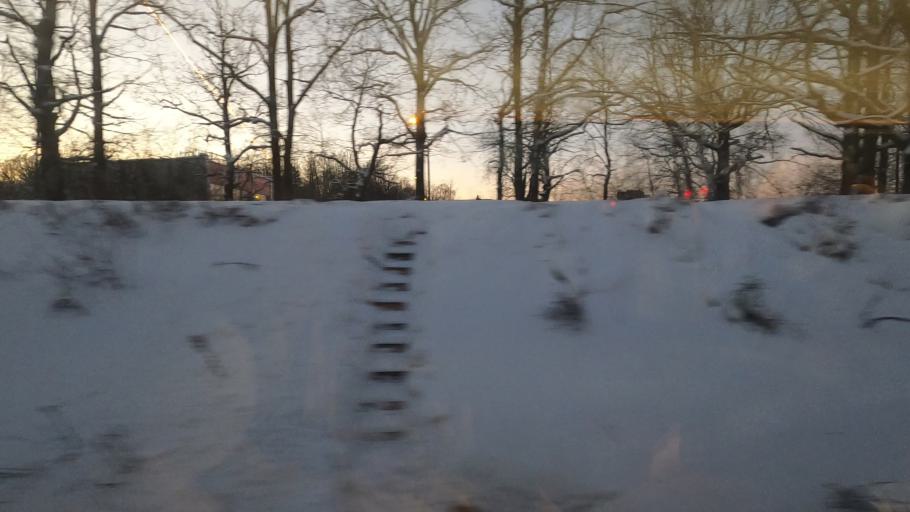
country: RU
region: Moskovskaya
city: Lugovaya
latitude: 56.0455
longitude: 37.4917
